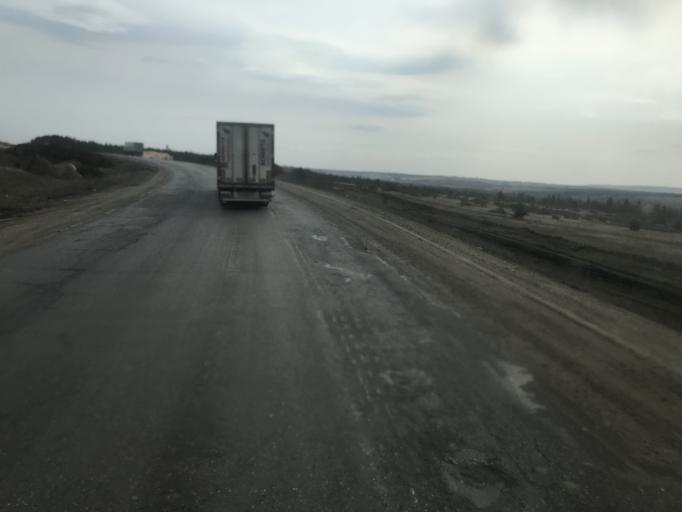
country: RU
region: Ulyanovsk
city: Novospasskoye
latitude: 53.1500
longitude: 47.6515
